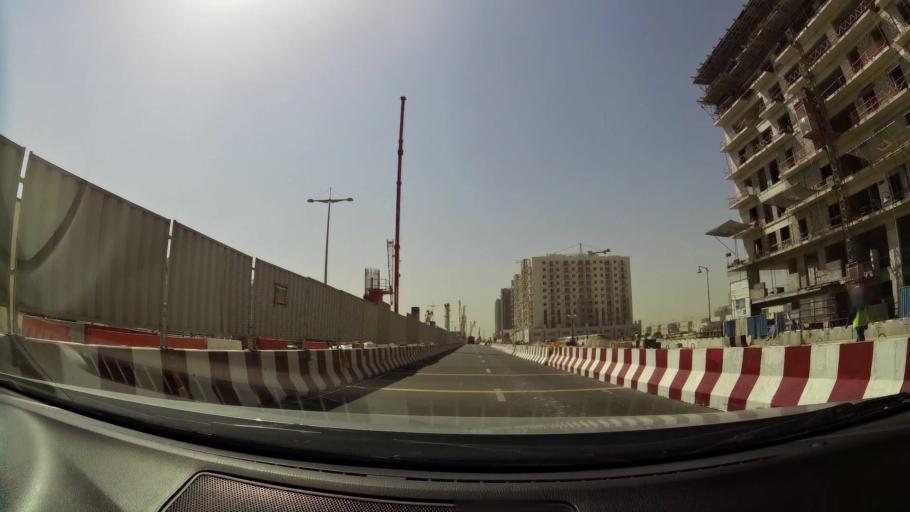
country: AE
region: Dubai
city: Dubai
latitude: 25.0289
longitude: 55.1542
